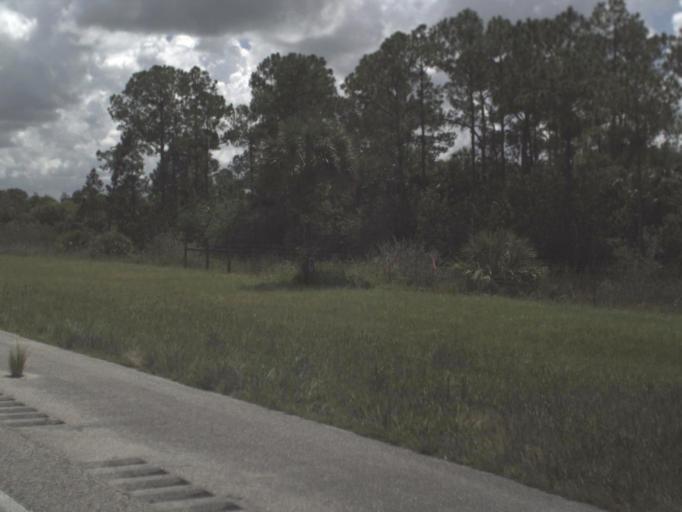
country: US
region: Florida
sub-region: Collier County
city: Orangetree
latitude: 26.1529
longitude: -81.5264
